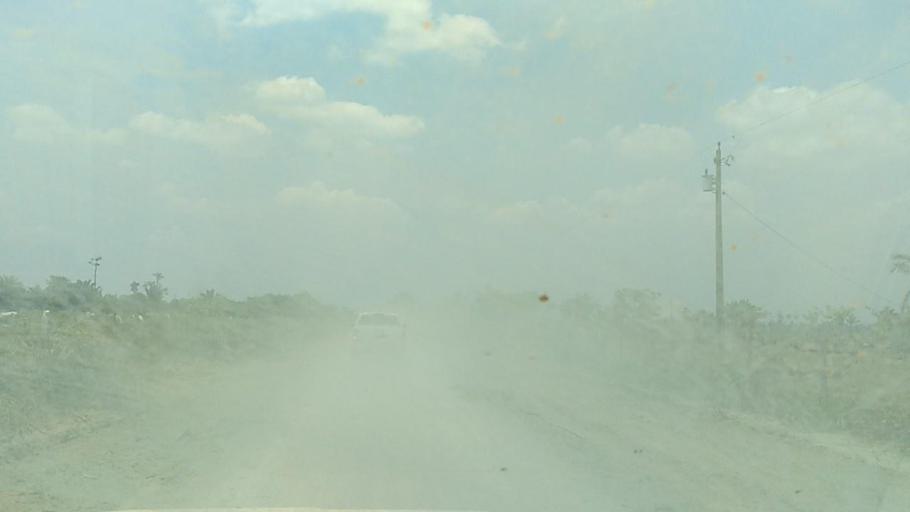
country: BR
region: Rondonia
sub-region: Porto Velho
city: Porto Velho
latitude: -8.7291
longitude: -63.2903
